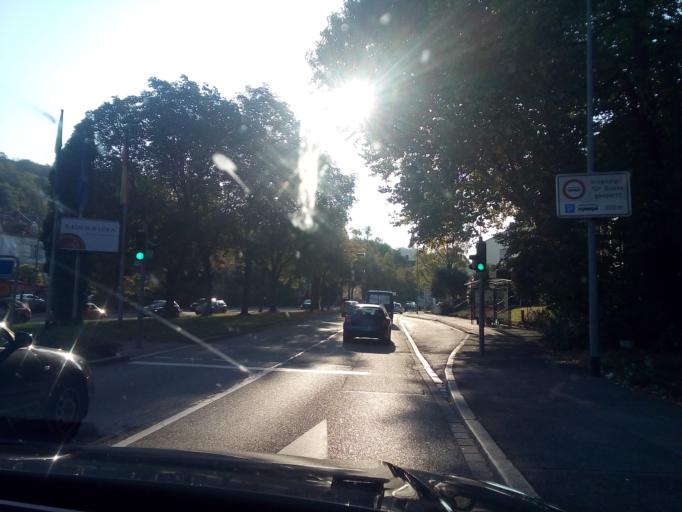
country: DE
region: Baden-Wuerttemberg
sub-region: Karlsruhe Region
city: Baden-Baden
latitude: 48.7718
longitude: 8.2254
